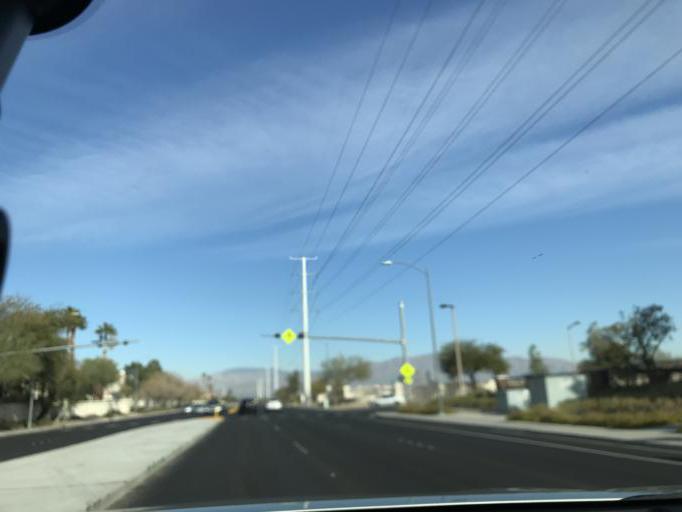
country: US
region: Nevada
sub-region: Clark County
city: Spring Valley
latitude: 36.2094
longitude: -115.2606
